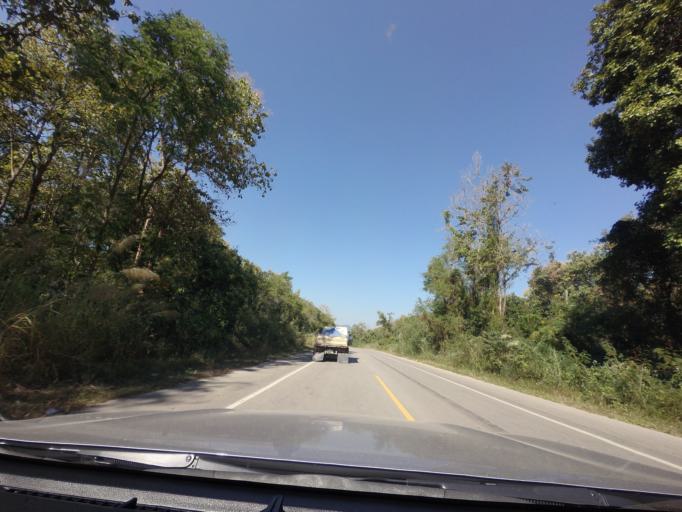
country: TH
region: Lampang
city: Mae Mo
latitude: 18.4972
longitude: 99.6471
